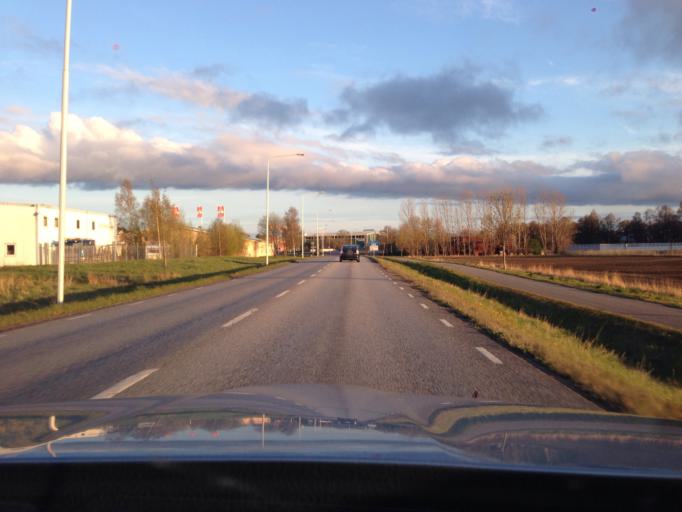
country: SE
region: Soedermanland
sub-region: Trosa Kommun
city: Trosa
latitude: 58.9081
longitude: 17.5499
